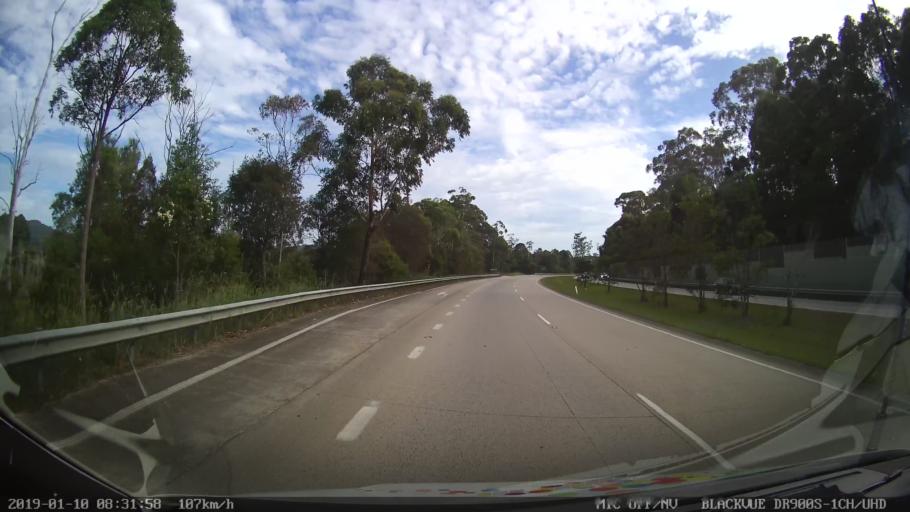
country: AU
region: New South Wales
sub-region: Coffs Harbour
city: Boambee
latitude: -30.3490
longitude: 153.0652
